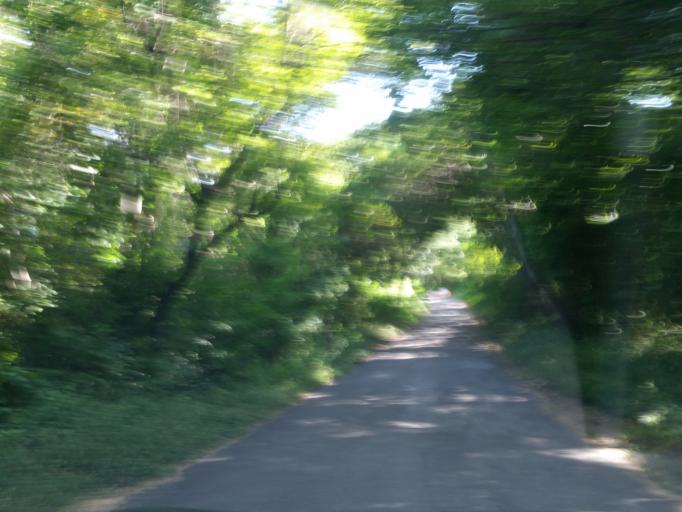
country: NI
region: Masaya
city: Catarina
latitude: 11.9329
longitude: -86.0566
